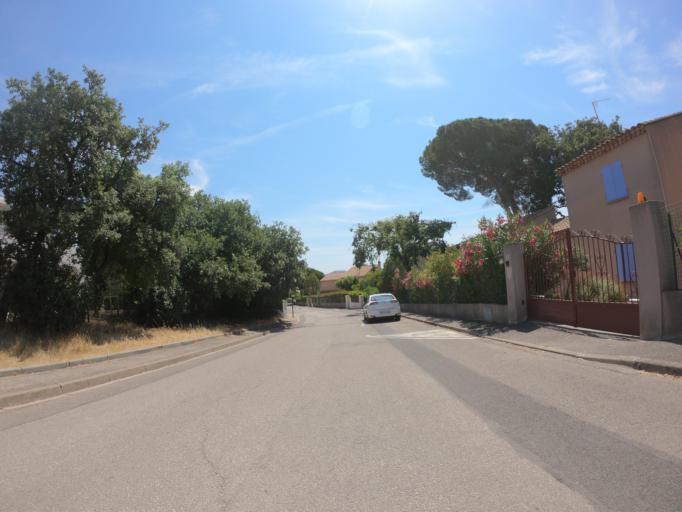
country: FR
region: Provence-Alpes-Cote d'Azur
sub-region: Departement du Var
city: La Garde
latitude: 43.1165
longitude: 6.0003
